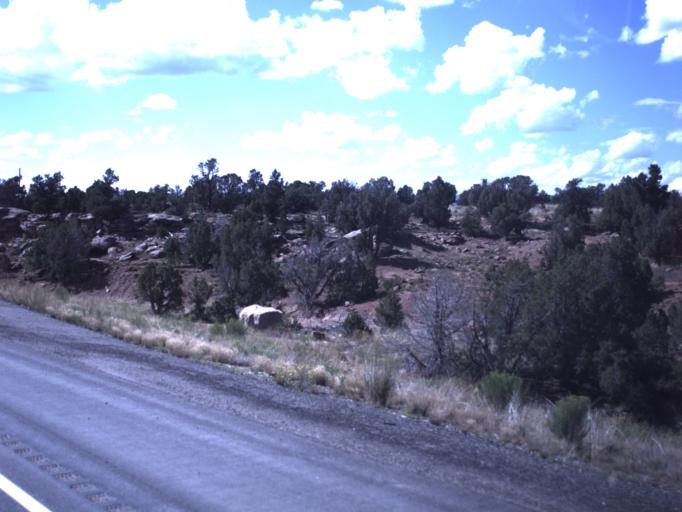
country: US
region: Utah
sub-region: Duchesne County
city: Duchesne
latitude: 40.2051
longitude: -110.8023
